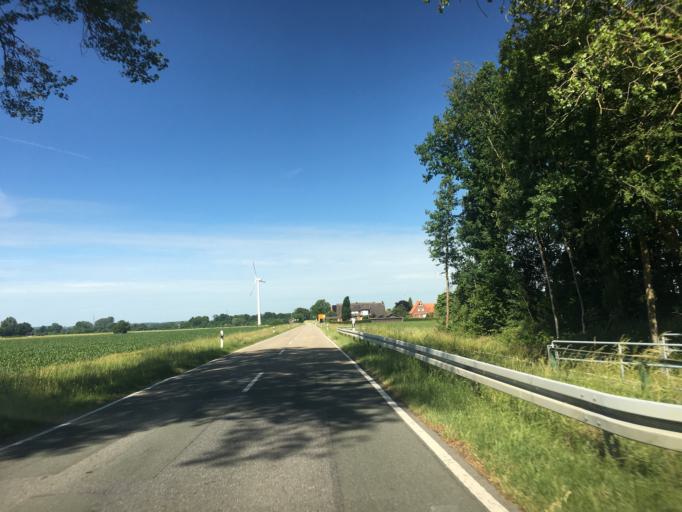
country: DE
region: North Rhine-Westphalia
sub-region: Regierungsbezirk Munster
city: Altenberge
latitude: 52.0161
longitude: 7.4505
